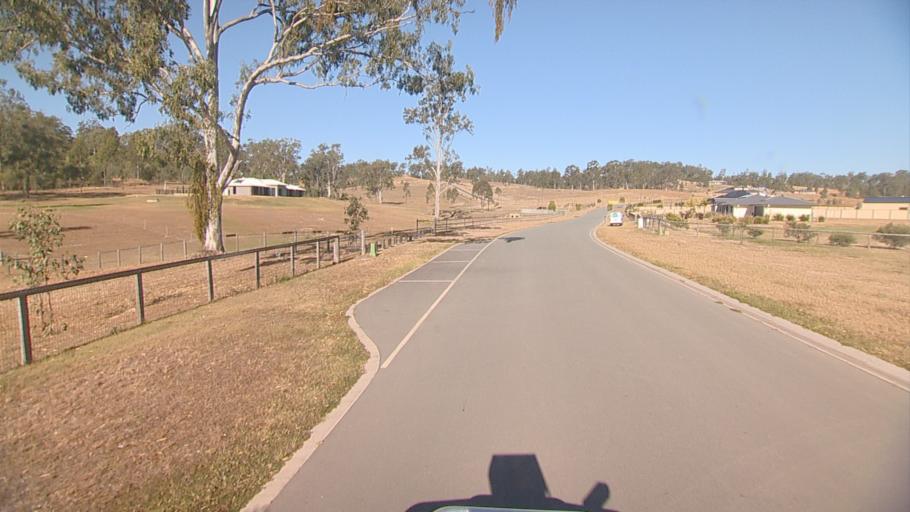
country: AU
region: Queensland
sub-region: Logan
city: Cedar Vale
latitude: -27.8698
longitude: 153.0556
